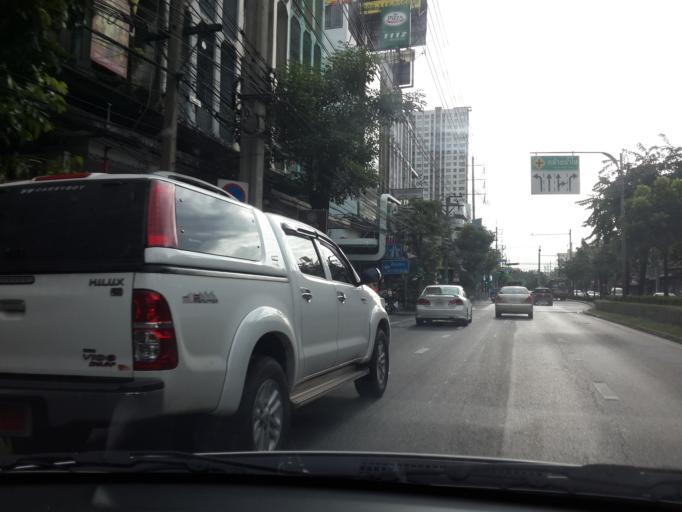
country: TH
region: Bangkok
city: Khlong Toei
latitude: 13.7128
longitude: 100.5853
